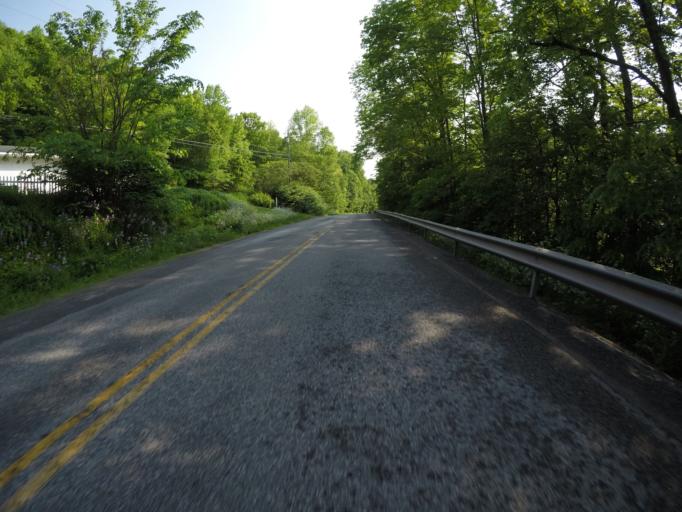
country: US
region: New York
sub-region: Delaware County
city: Stamford
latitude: 42.1380
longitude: -74.6626
